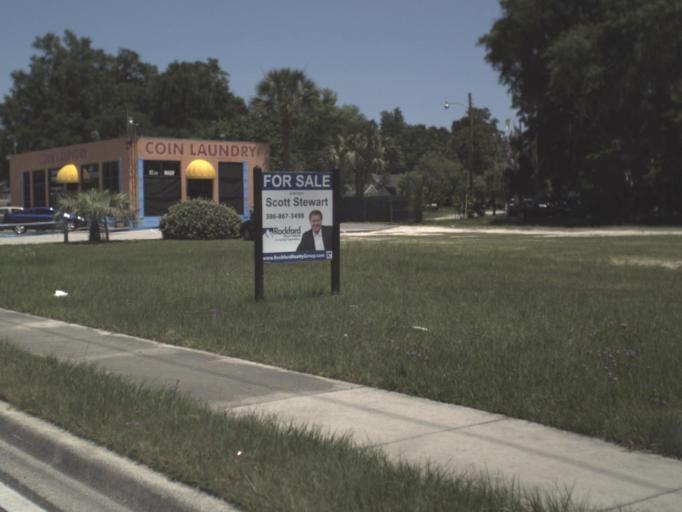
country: US
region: Florida
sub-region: Columbia County
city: Lake City
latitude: 30.1881
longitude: -82.6506
